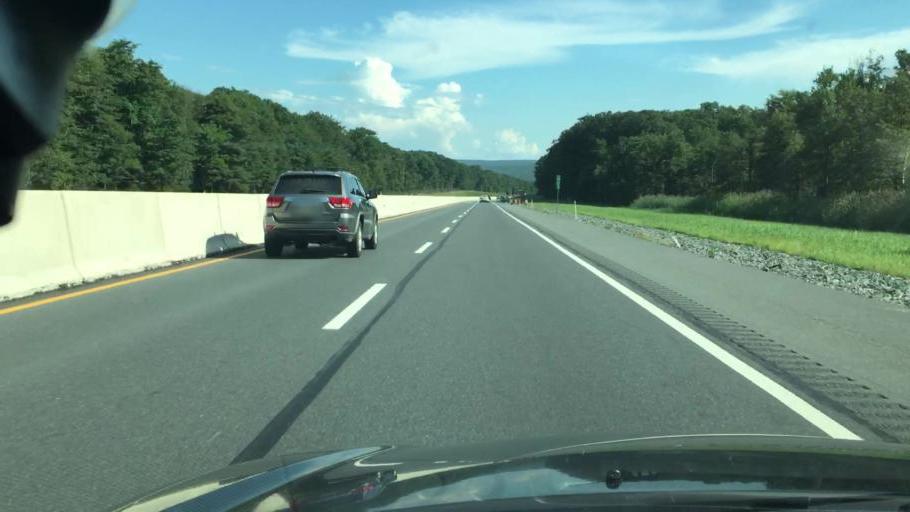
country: US
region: Pennsylvania
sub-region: Carbon County
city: Towamensing Trails
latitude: 41.0285
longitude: -75.6515
